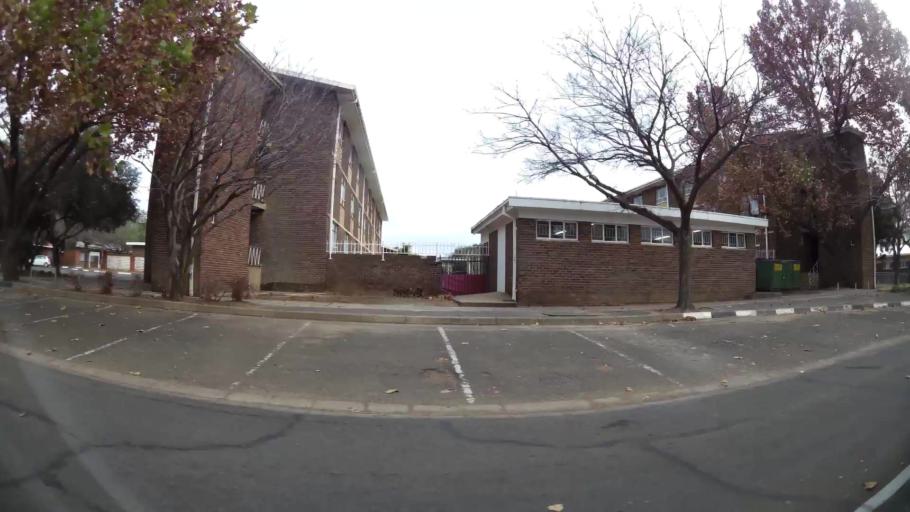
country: ZA
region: Orange Free State
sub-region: Mangaung Metropolitan Municipality
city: Bloemfontein
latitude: -29.1141
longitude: 26.1866
